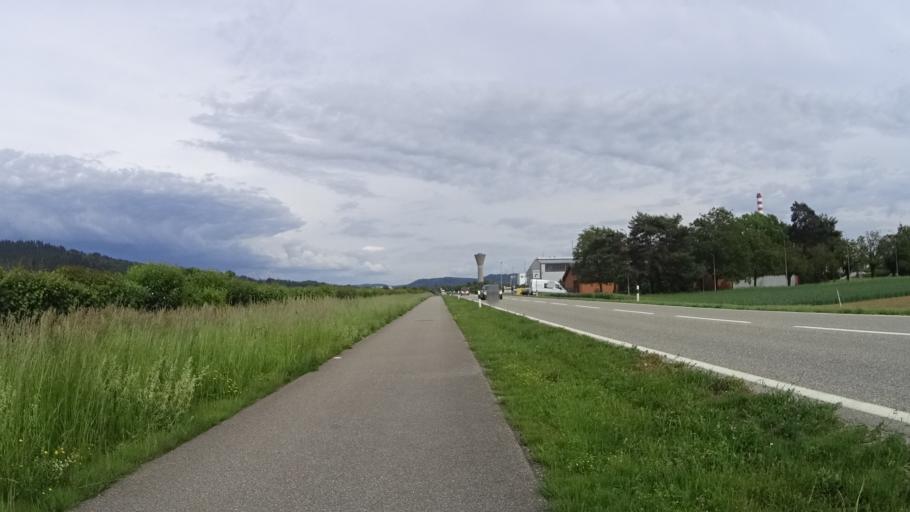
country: CH
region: Aargau
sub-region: Bezirk Rheinfelden
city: Stein
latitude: 47.5517
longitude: 7.9716
